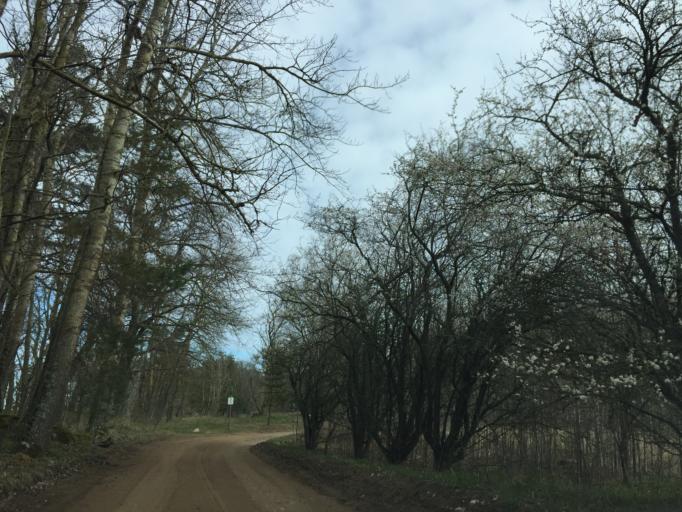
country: LV
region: Salacgrivas
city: Salacgriva
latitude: 57.5180
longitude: 24.3793
